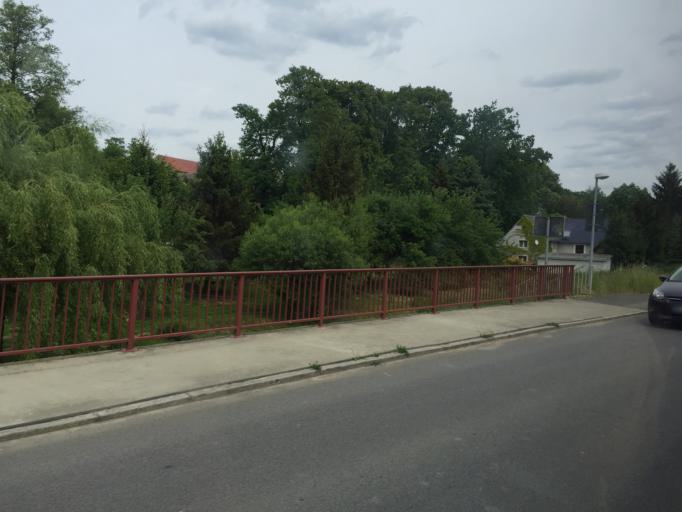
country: DE
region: Saxony
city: Markersdorf
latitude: 51.1470
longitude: 14.8865
